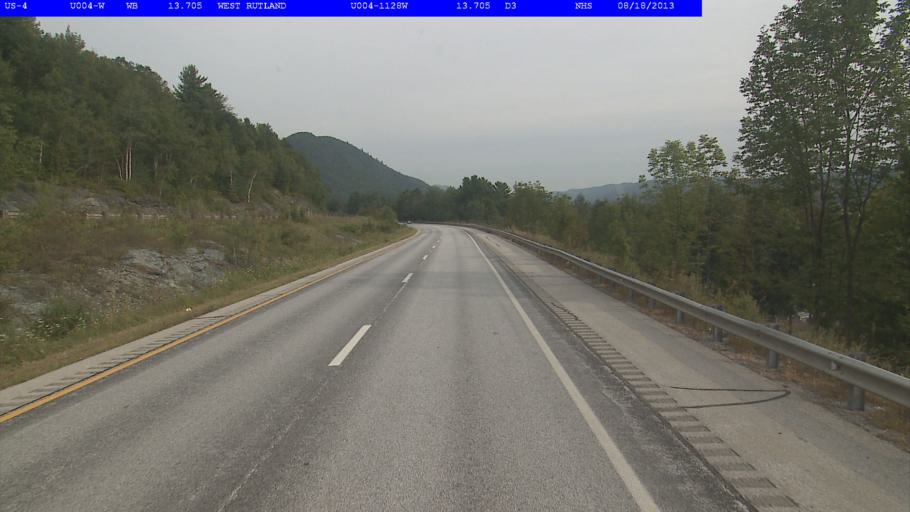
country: US
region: Vermont
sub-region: Rutland County
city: West Rutland
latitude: 43.5969
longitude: -73.0568
